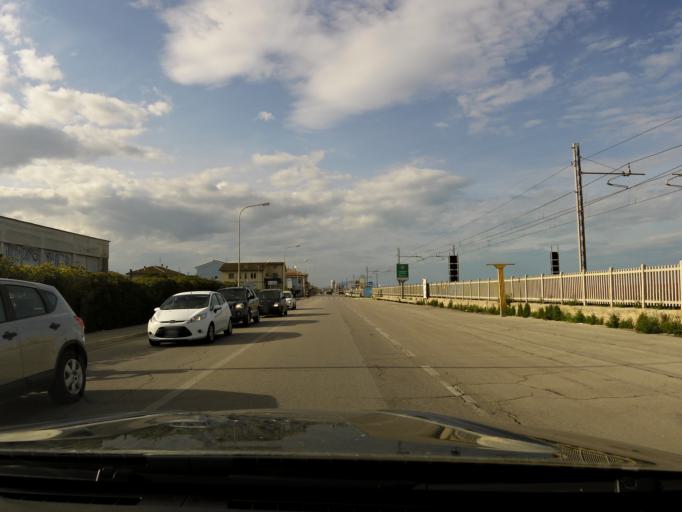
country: IT
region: The Marches
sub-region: Provincia di Macerata
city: Civitanova Marche
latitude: 43.3326
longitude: 13.7118
